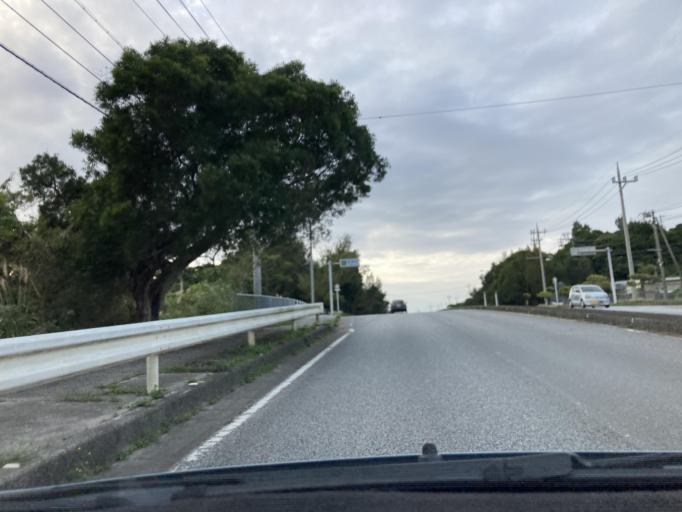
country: JP
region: Okinawa
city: Ishikawa
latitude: 26.4366
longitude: 127.8097
